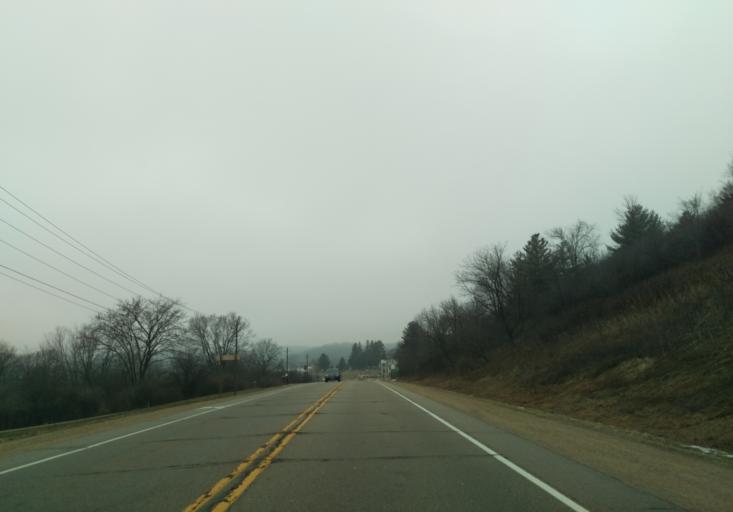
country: US
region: Wisconsin
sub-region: Dane County
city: Cross Plains
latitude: 43.1065
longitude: -89.6375
